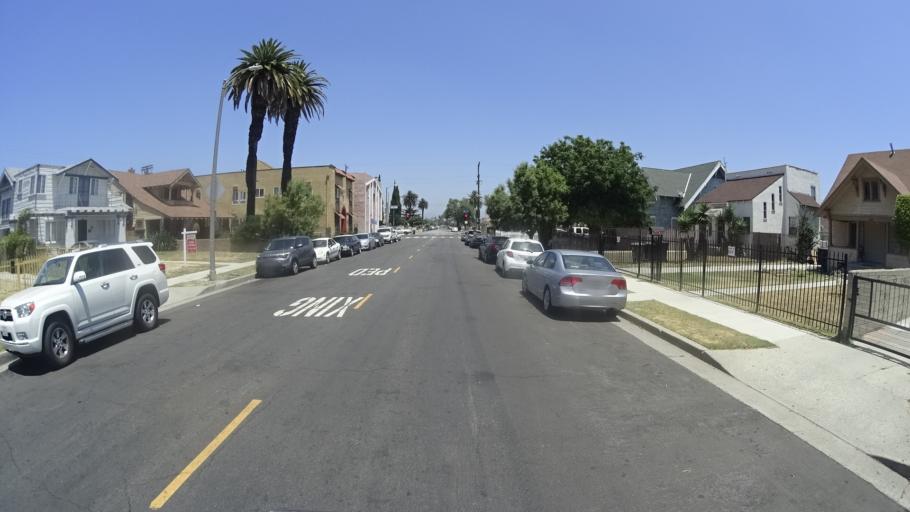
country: US
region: California
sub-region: Los Angeles County
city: View Park-Windsor Hills
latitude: 33.9993
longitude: -118.3138
